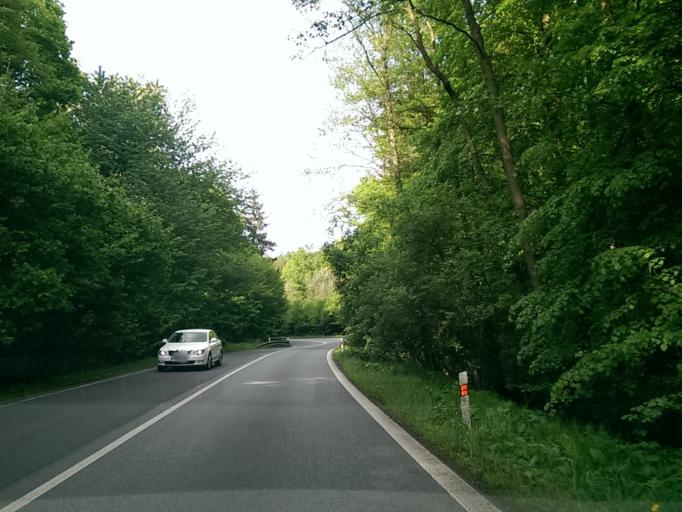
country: CZ
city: Duba
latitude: 50.5279
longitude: 14.5200
